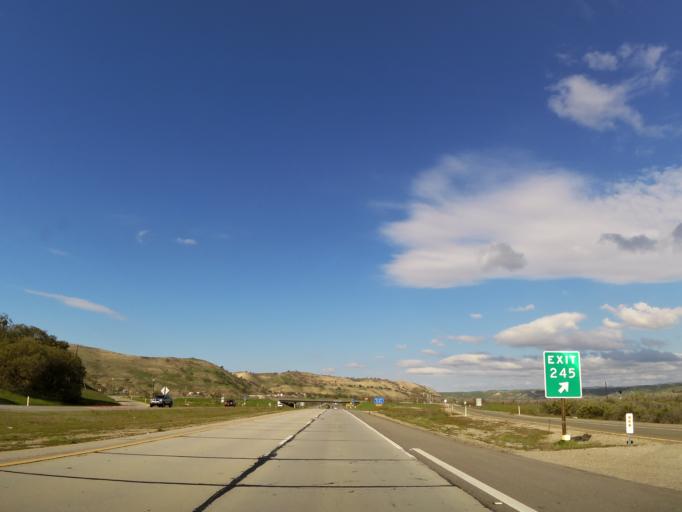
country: US
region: California
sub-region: San Luis Obispo County
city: San Miguel
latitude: 35.8120
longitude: -120.7525
